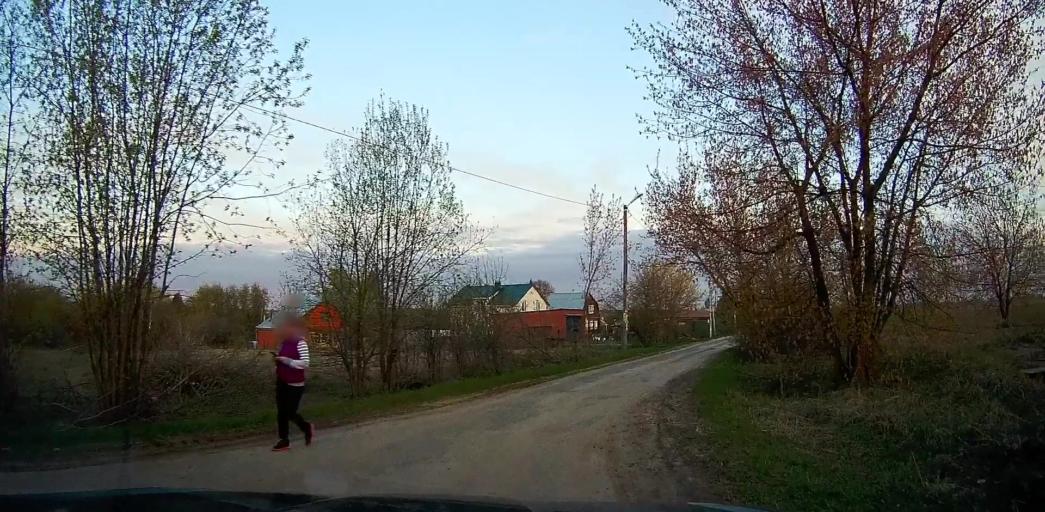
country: RU
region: Moskovskaya
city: Peski
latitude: 55.2316
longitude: 38.7326
